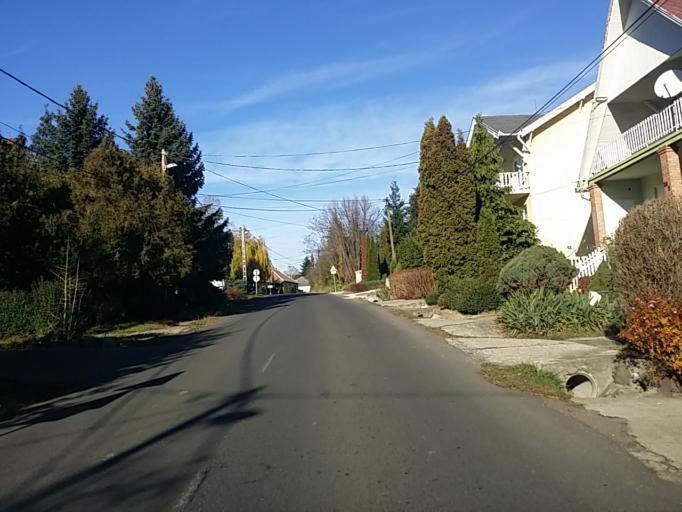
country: HU
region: Heves
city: Abasar
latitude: 47.8225
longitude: 19.9754
